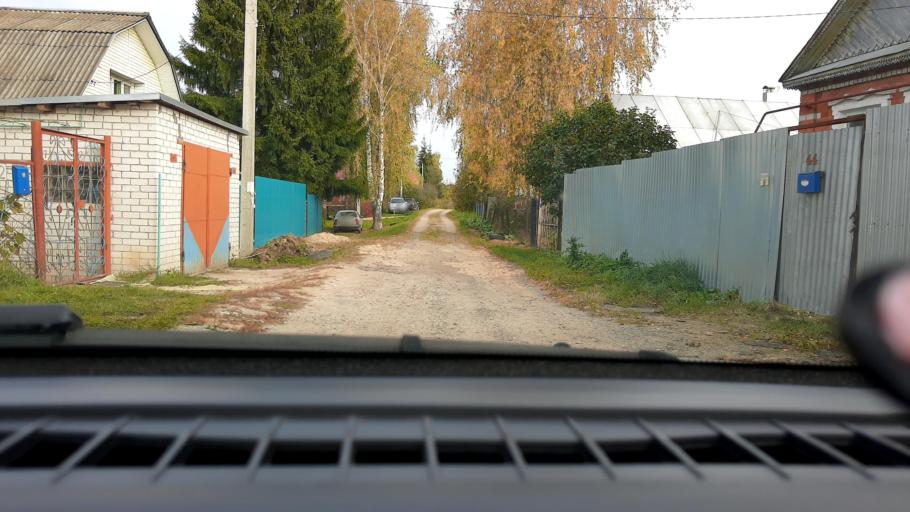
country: RU
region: Nizjnij Novgorod
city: Nizhniy Novgorod
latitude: 56.1972
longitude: 43.9636
